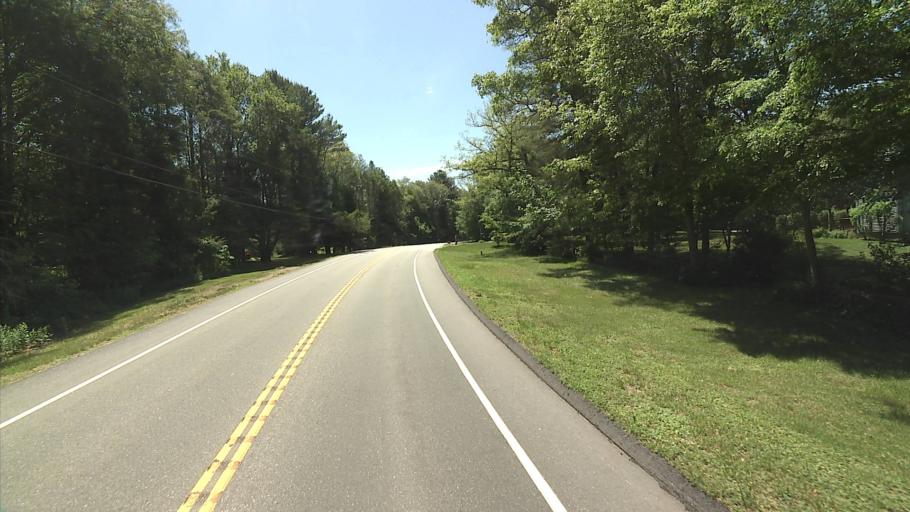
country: US
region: Rhode Island
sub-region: Washington County
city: Hopkinton
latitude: 41.5321
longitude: -71.8368
